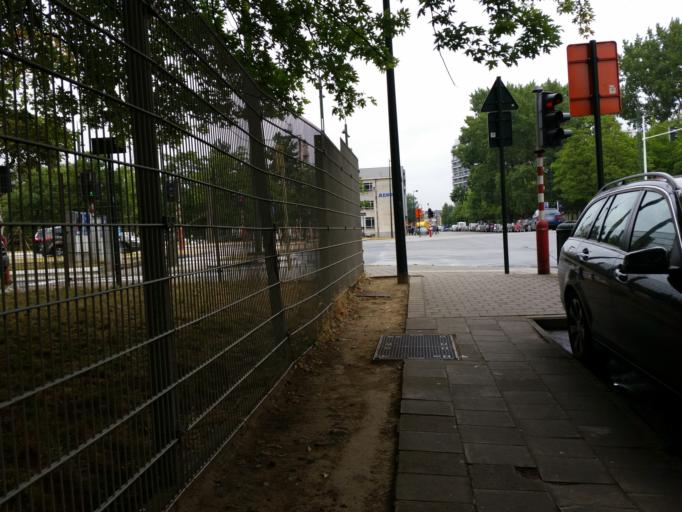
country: BE
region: Brussels Capital
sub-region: Bruxelles-Capitale
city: Brussels
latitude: 50.8613
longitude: 4.3534
